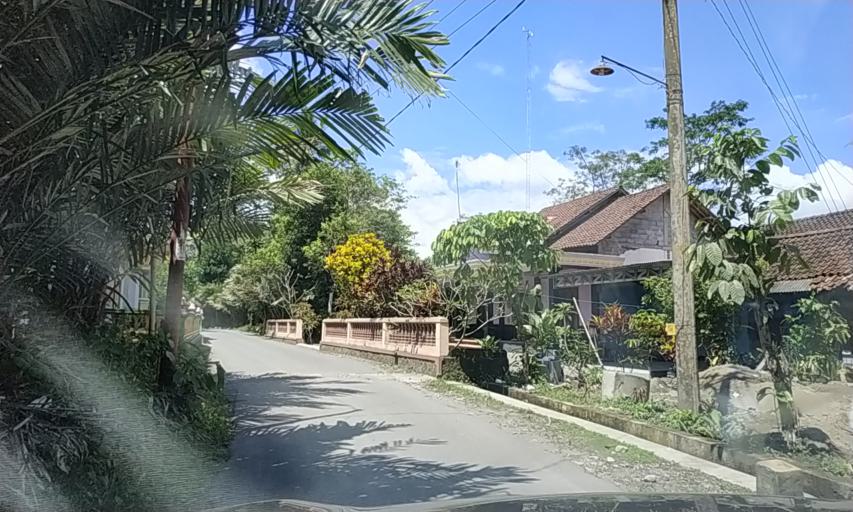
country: ID
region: Central Java
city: Muntilan
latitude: -7.6030
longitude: 110.3561
